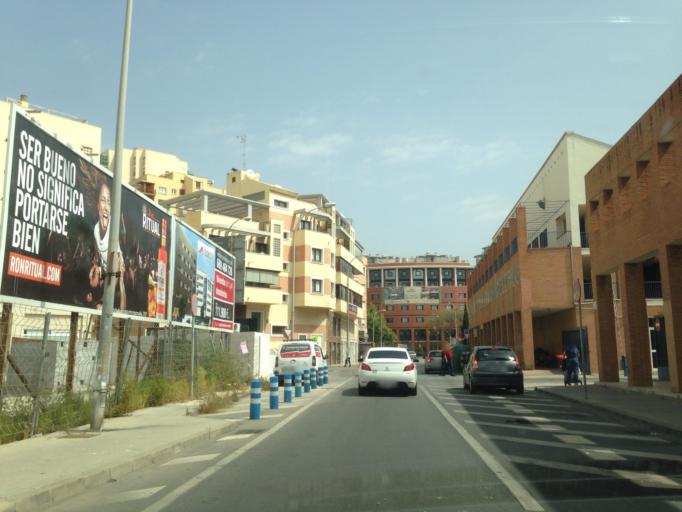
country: ES
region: Andalusia
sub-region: Provincia de Malaga
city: Malaga
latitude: 36.7122
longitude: -4.4350
